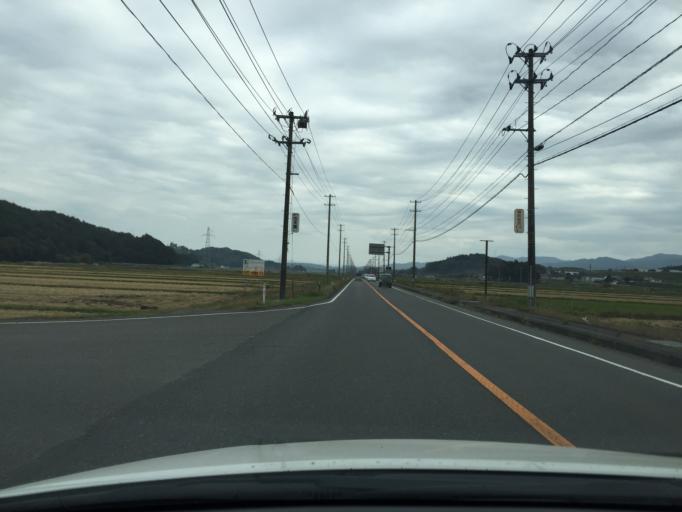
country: JP
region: Fukushima
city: Ishikawa
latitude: 37.0869
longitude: 140.2661
